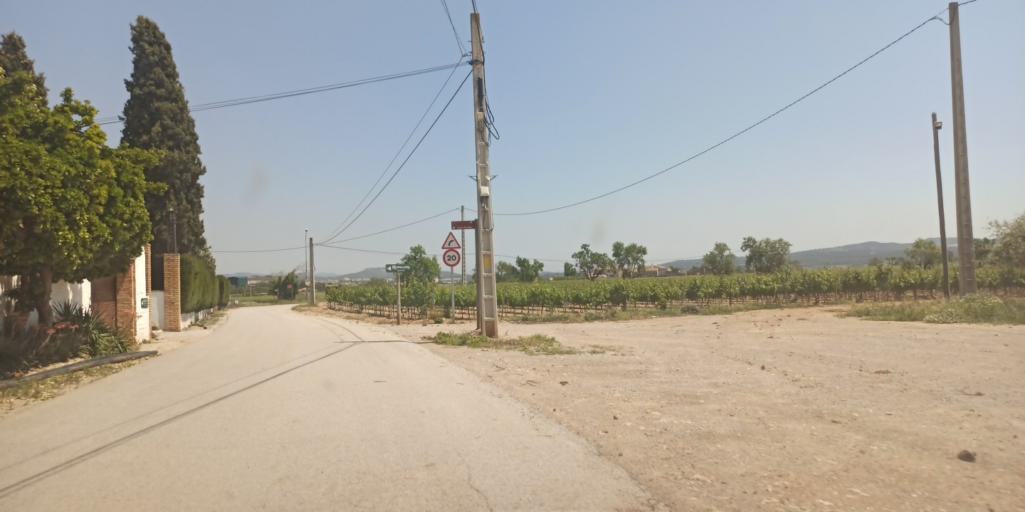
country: ES
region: Catalonia
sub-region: Provincia de Barcelona
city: Vilobi del Penedes
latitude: 41.3538
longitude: 1.6469
